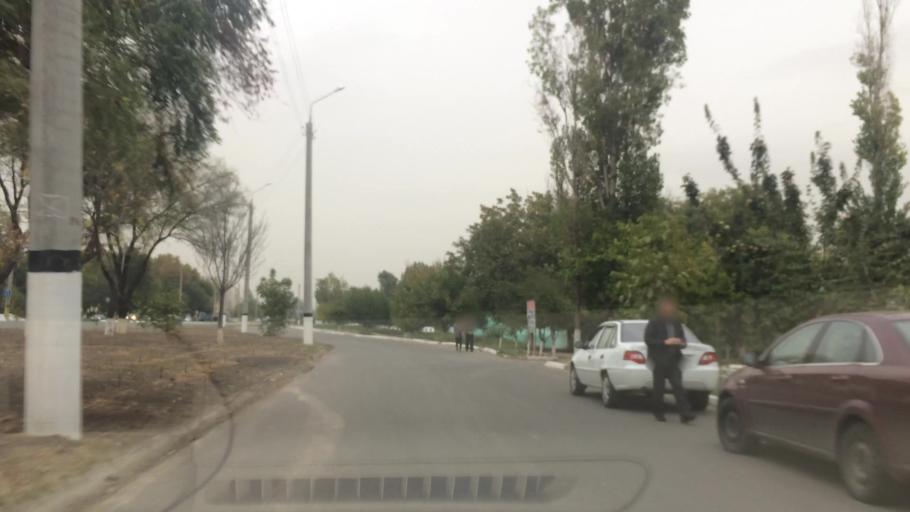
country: UZ
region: Toshkent
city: Salor
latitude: 41.3117
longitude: 69.3479
